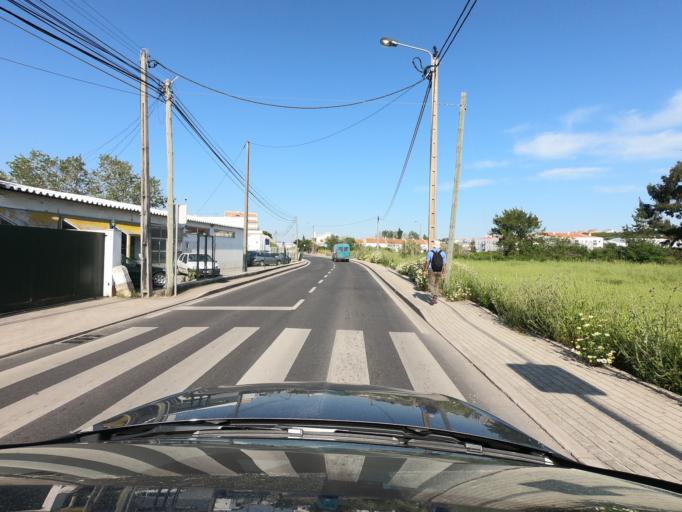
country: PT
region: Lisbon
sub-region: Cascais
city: Alcabideche
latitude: 38.7386
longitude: -9.3730
